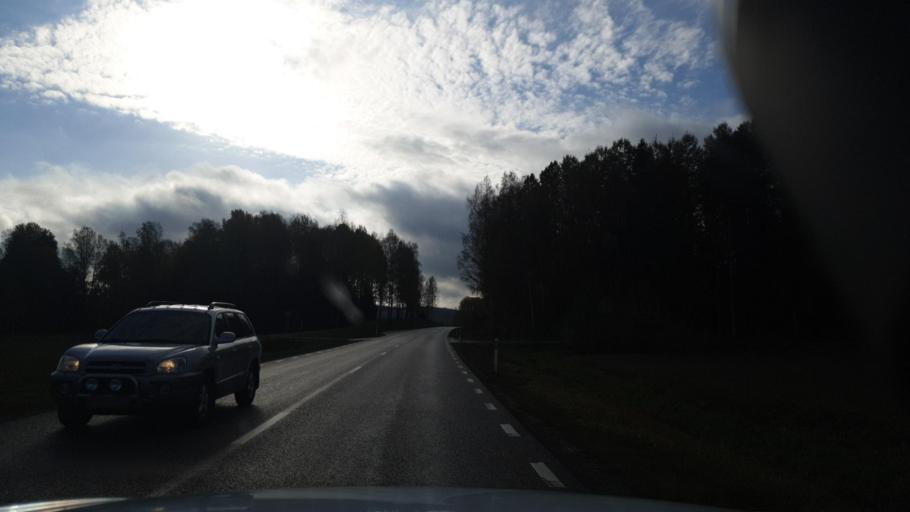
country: SE
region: Vaermland
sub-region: Arvika Kommun
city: Arvika
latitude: 59.4771
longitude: 12.7702
